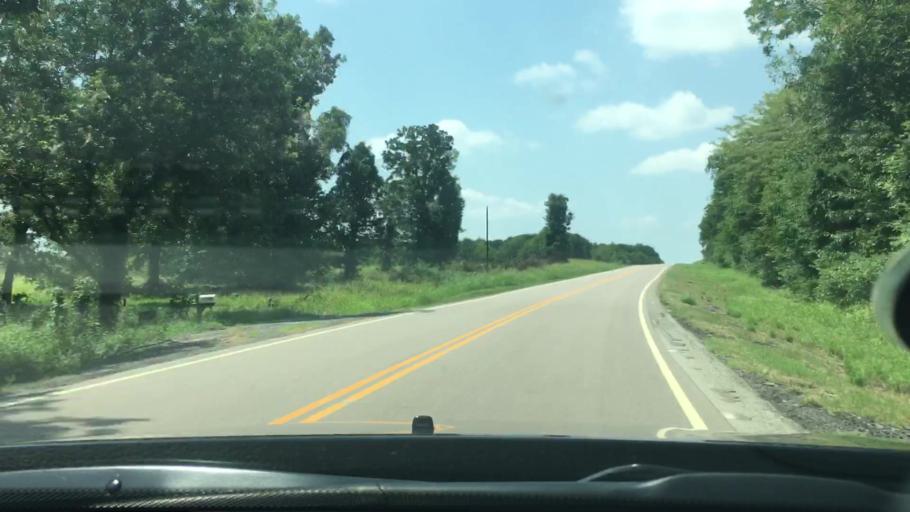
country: US
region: Oklahoma
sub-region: Coal County
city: Coalgate
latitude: 34.3669
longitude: -96.3349
